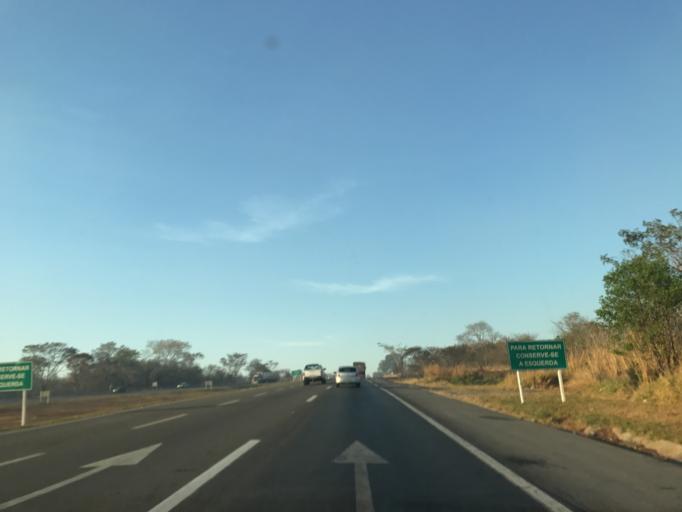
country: BR
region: Goias
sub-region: Goianapolis
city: Goianapolis
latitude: -16.5436
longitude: -49.1507
